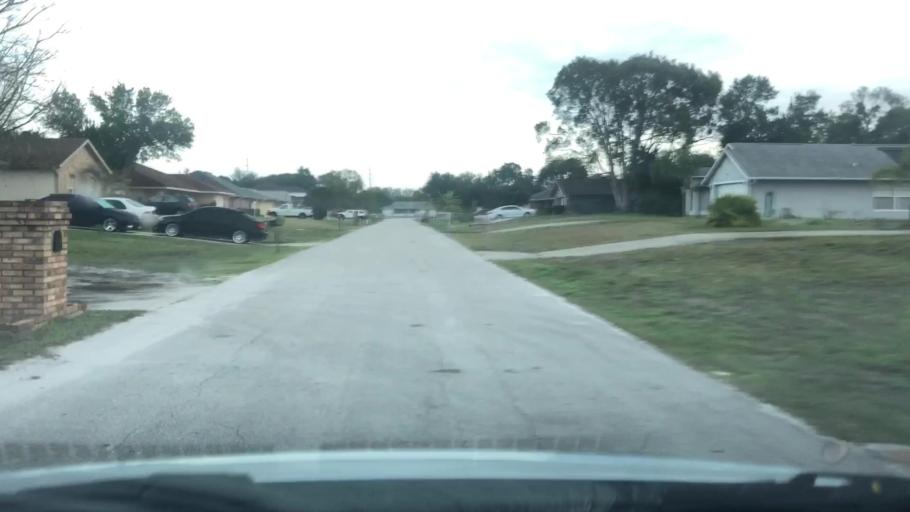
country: US
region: Florida
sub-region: Volusia County
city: Deltona
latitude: 28.8776
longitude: -81.2421
